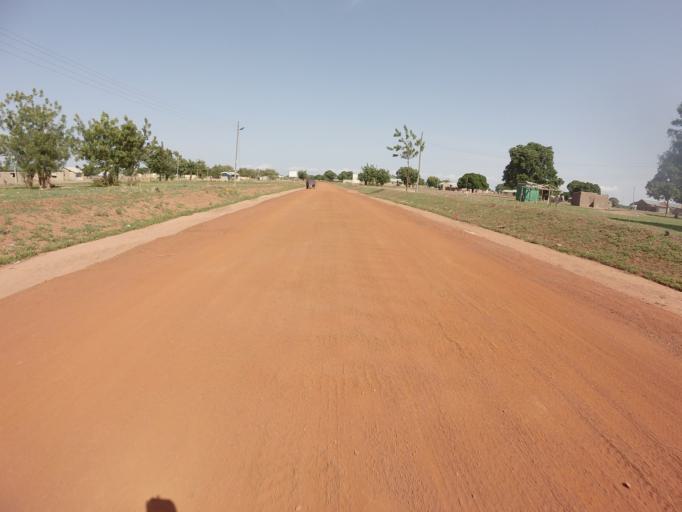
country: GH
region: Upper East
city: Bawku
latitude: 10.8376
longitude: -0.1771
